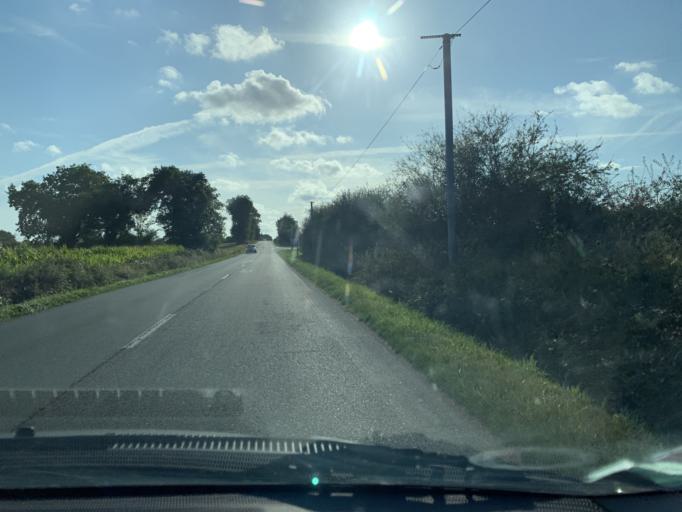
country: FR
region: Brittany
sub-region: Departement du Morbihan
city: Ambon
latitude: 47.5553
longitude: -2.5306
